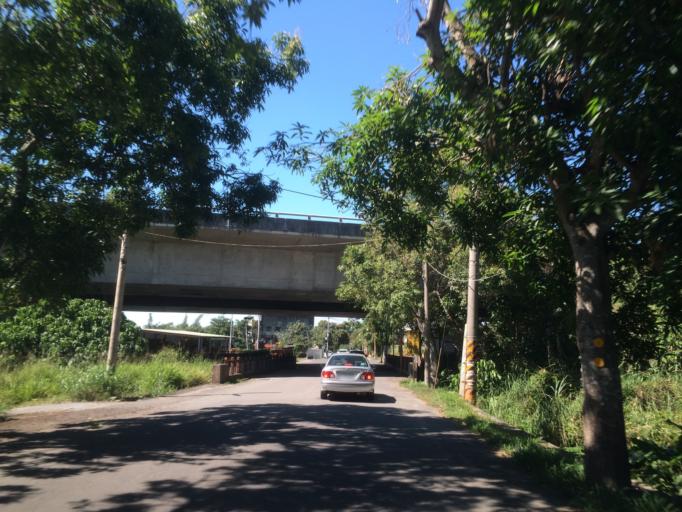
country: TW
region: Taiwan
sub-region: Yunlin
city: Douliu
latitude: 23.7015
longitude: 120.6037
